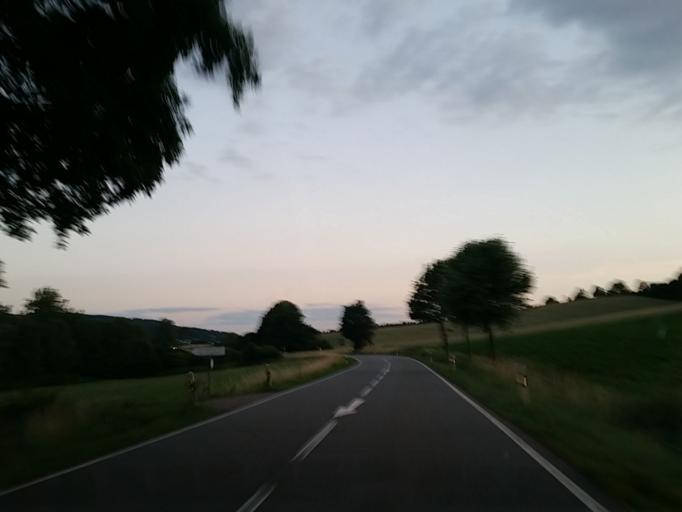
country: DE
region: Saarland
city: Wadern
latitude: 49.5009
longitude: 6.8536
